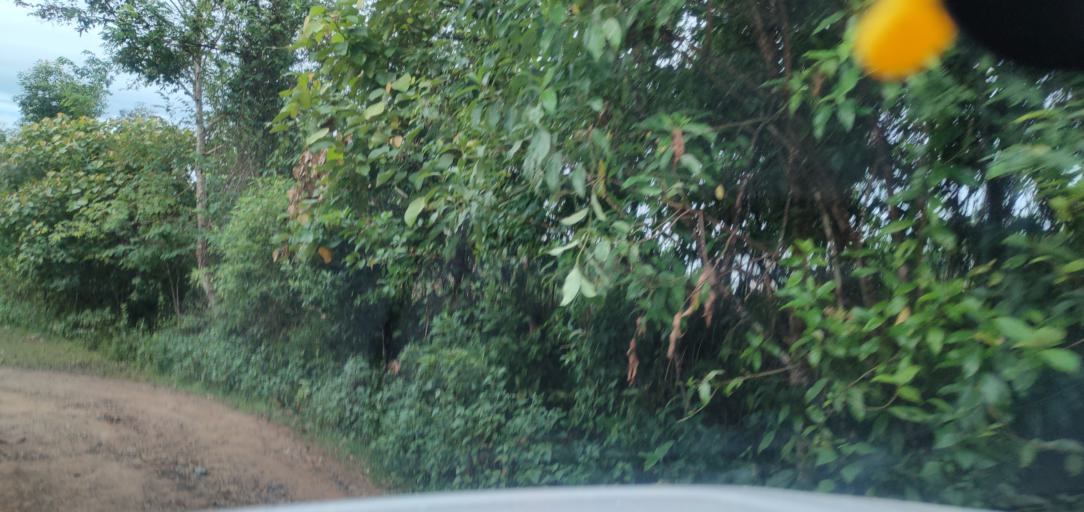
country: LA
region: Phongsali
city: Phongsali
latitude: 21.4318
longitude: 102.2610
